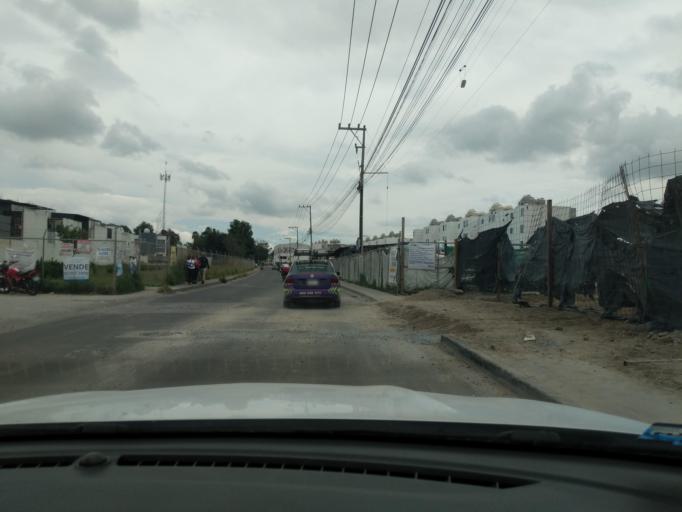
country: MX
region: Jalisco
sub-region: Zapopan
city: La Cuchilla (Extramuros de Tesistan)
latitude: 20.7837
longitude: -103.4759
